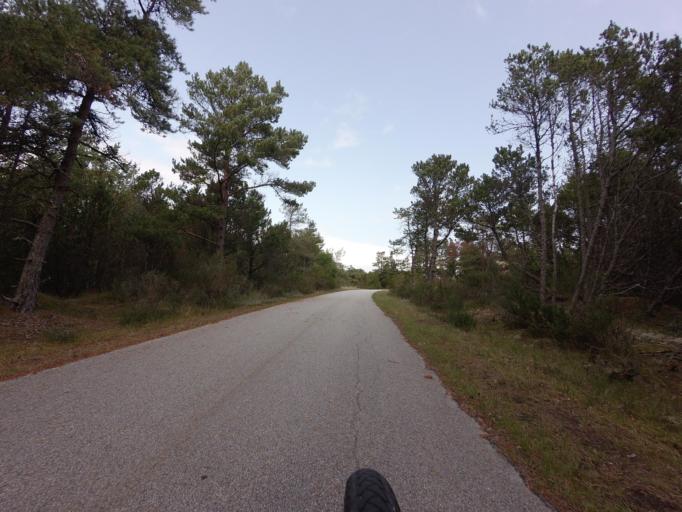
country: DK
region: North Denmark
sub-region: Frederikshavn Kommune
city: Strandby
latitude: 57.6423
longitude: 10.4369
